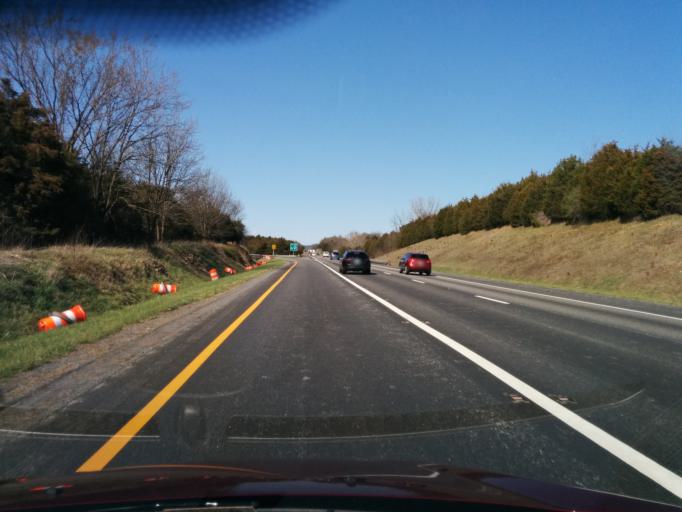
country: US
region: Virginia
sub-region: Rockbridge County
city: East Lexington
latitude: 37.7903
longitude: -79.3976
